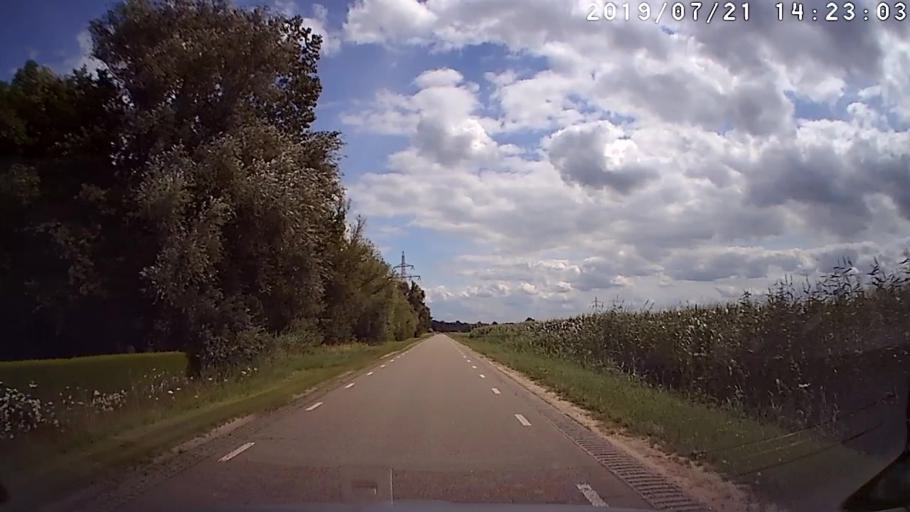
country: NL
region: Overijssel
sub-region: Gemeente Raalte
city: Heino
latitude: 52.4583
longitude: 6.1684
